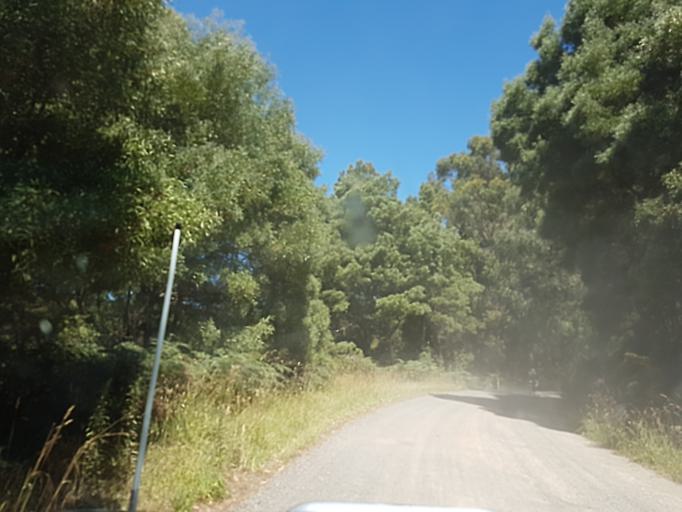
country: AU
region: Victoria
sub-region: Colac-Otway
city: Apollo Bay
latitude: -38.6383
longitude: 143.3067
